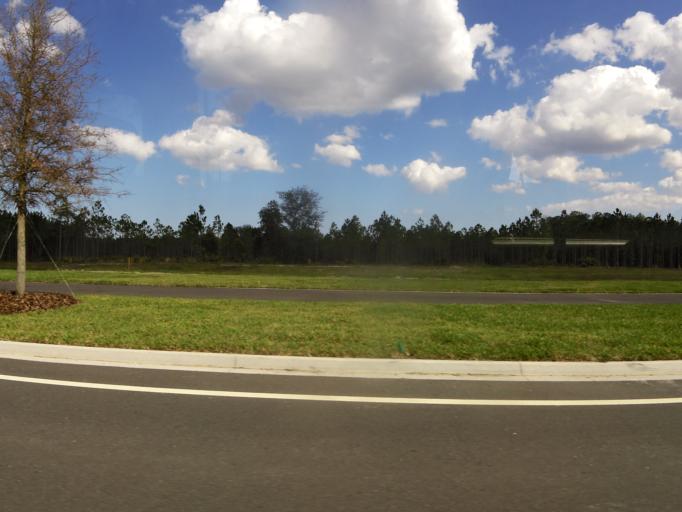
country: US
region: Florida
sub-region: Saint Johns County
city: Palm Valley
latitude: 30.1996
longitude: -81.5072
